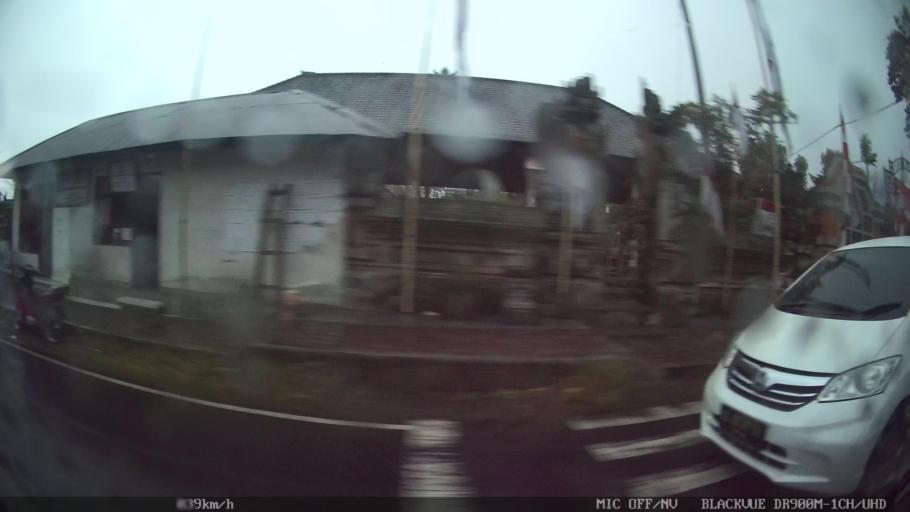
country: ID
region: Bali
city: Banjar Taro Kelod
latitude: -8.3238
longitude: 115.2946
